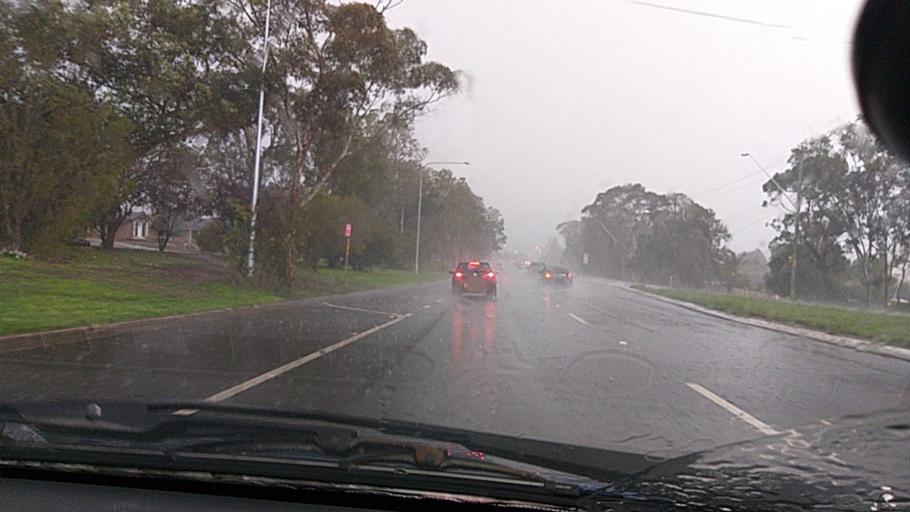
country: AU
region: New South Wales
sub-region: Camden
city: Camden South
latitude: -34.0866
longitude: 150.6952
